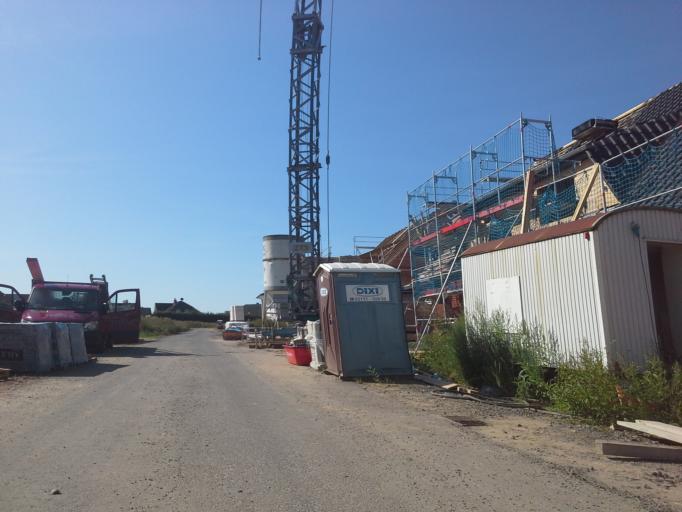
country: DE
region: Lower Saxony
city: Lauenau
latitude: 52.2810
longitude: 9.3723
